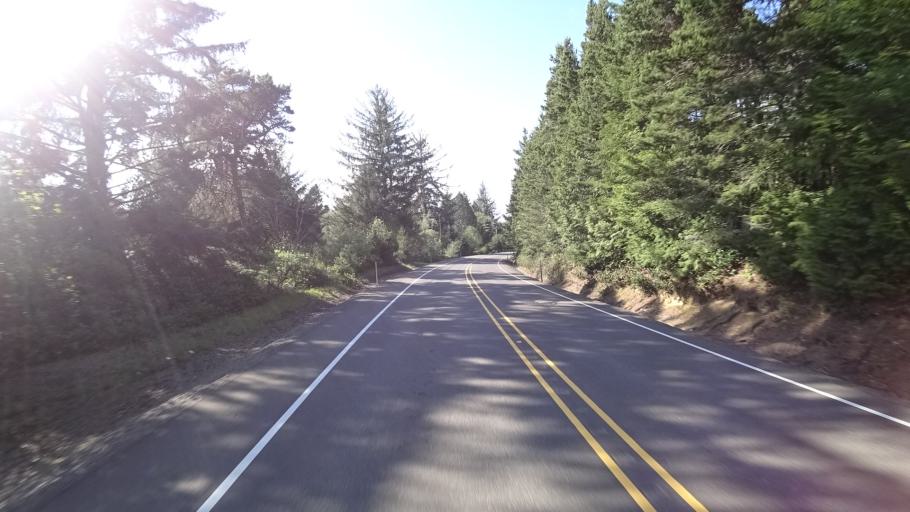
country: US
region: Oregon
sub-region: Lane County
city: Florence
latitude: 44.0775
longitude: -124.1045
